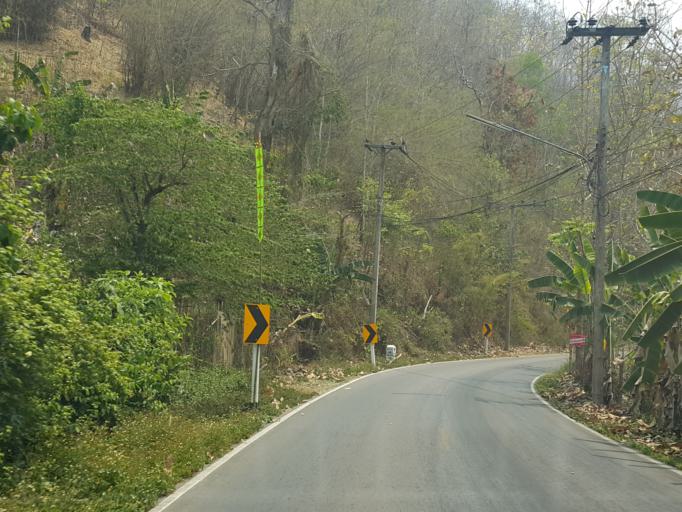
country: TH
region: Chiang Mai
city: Mae Taeng
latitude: 19.0023
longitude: 98.8879
